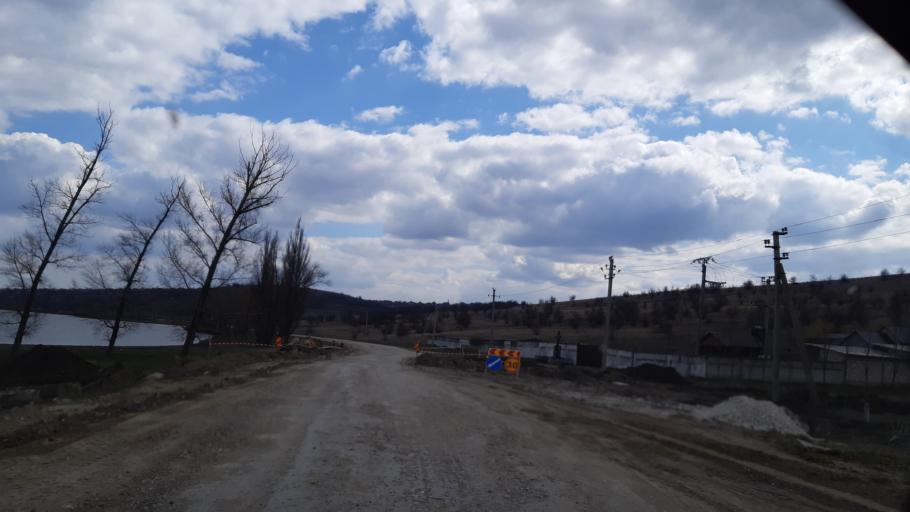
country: MD
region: Laloveni
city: Ialoveni
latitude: 46.8841
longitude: 28.7375
